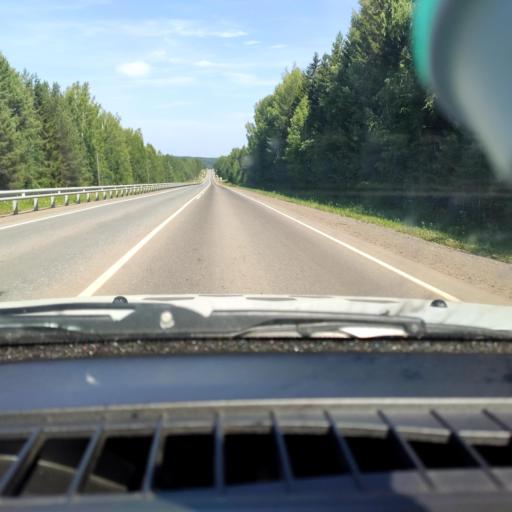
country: RU
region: Perm
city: Nytva
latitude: 57.8498
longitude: 55.1335
